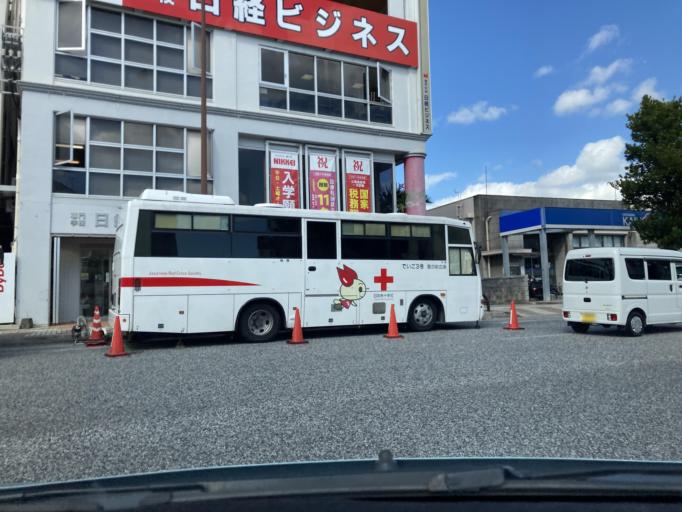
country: JP
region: Okinawa
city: Okinawa
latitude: 26.3292
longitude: 127.7945
